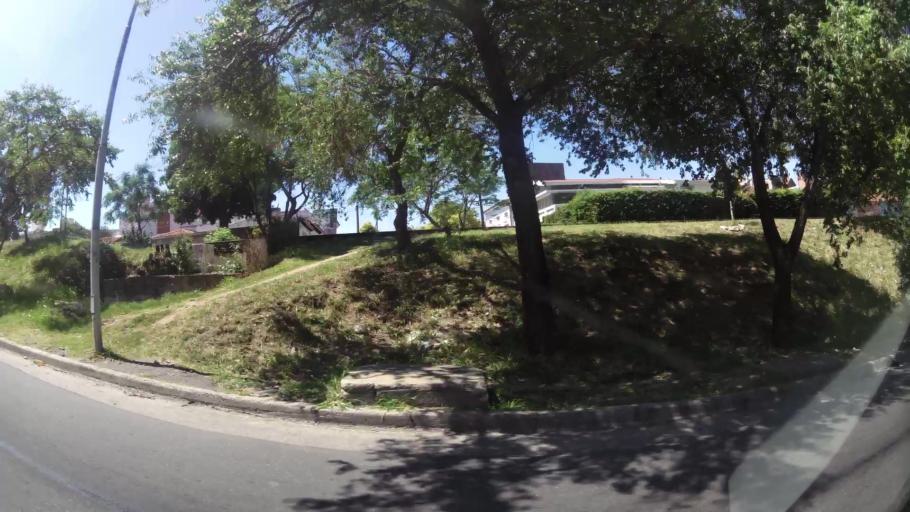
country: AR
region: Cordoba
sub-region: Departamento de Capital
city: Cordoba
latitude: -31.4033
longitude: -64.1889
